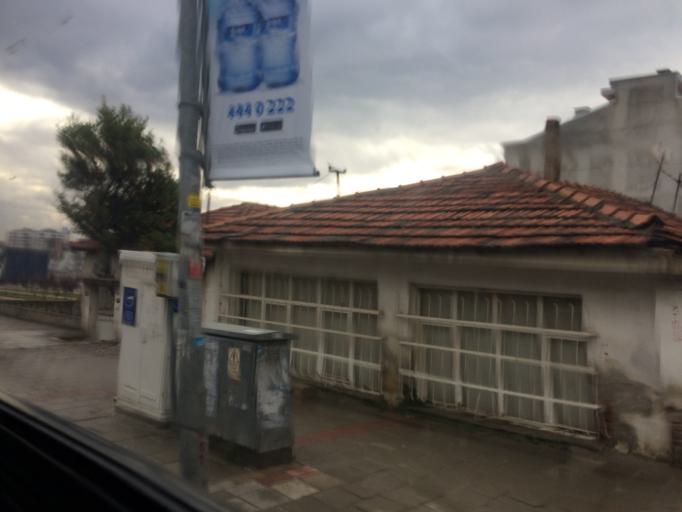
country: TR
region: Izmir
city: Karsiyaka
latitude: 38.4970
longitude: 27.0587
